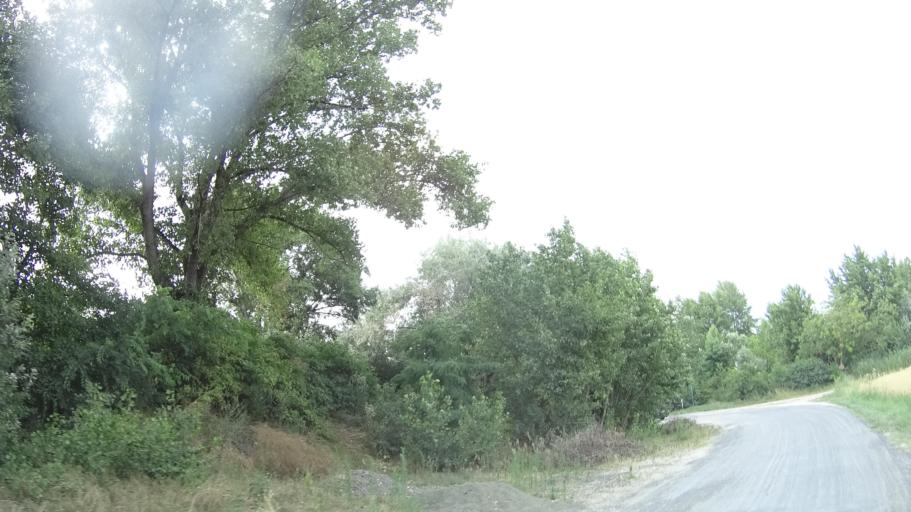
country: HU
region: Pest
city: Delegyhaza
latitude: 47.2556
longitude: 19.1073
